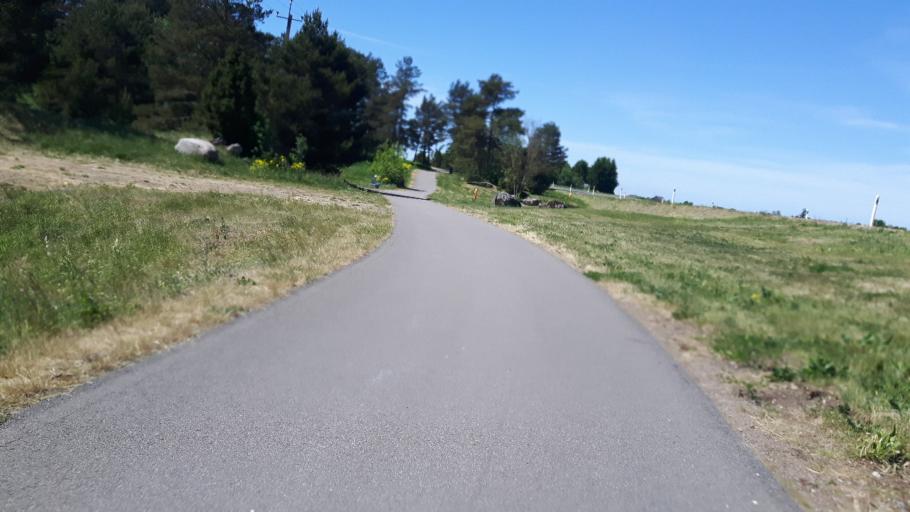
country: EE
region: Harju
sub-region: Kuusalu vald
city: Kuusalu
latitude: 59.4522
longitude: 25.4236
